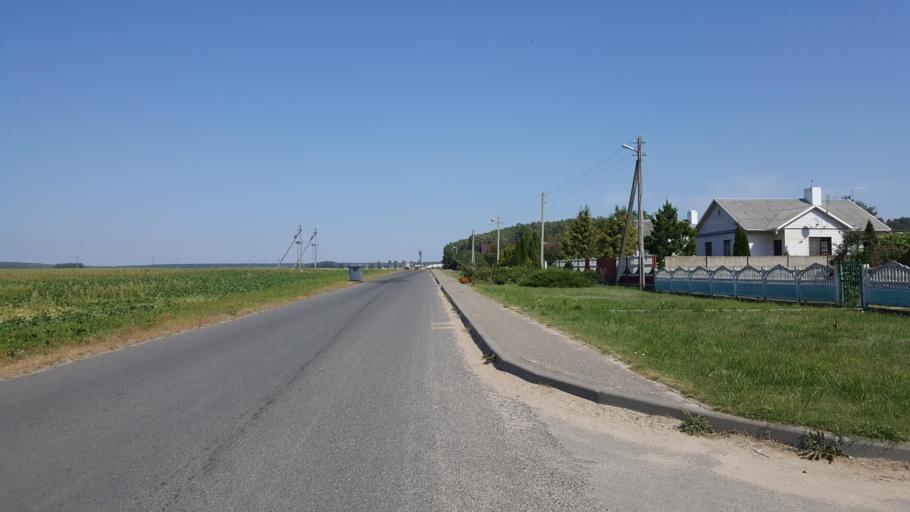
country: BY
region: Brest
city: Vysokaye
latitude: 52.4047
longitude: 23.4544
